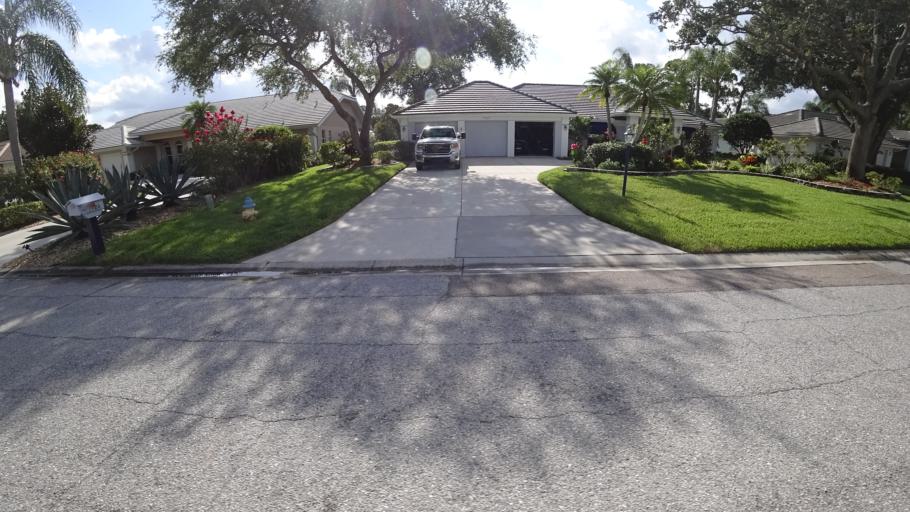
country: US
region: Florida
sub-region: Sarasota County
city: Desoto Lakes
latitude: 27.4019
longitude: -82.4855
